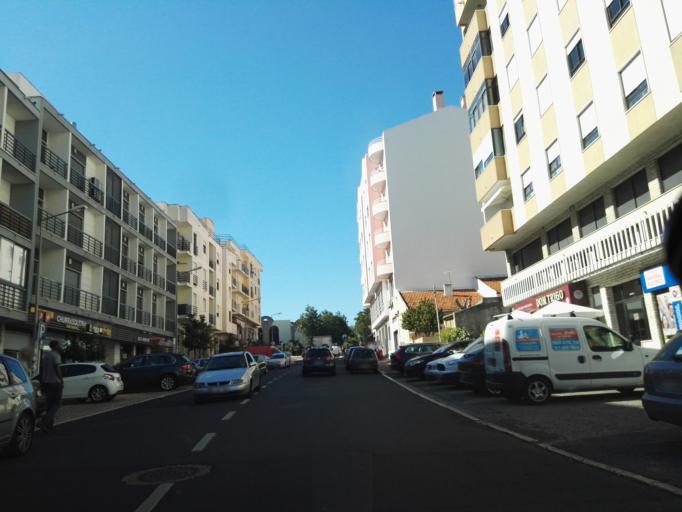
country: PT
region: Lisbon
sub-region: Loures
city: Sacavem
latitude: 38.7899
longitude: -9.1219
